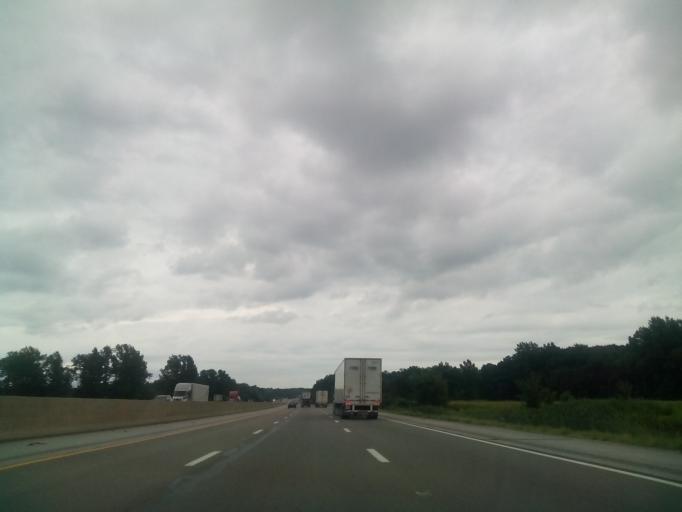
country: US
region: Ohio
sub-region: Erie County
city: Huron
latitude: 41.3262
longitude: -82.5178
